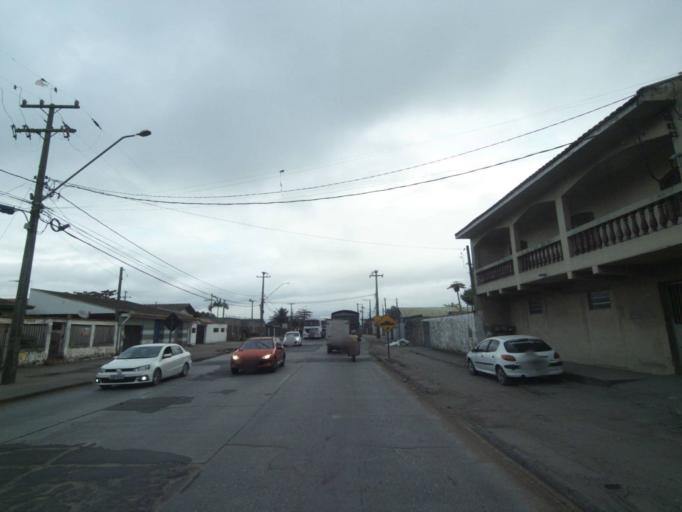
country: BR
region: Parana
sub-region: Paranagua
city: Paranagua
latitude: -25.5195
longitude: -48.5433
